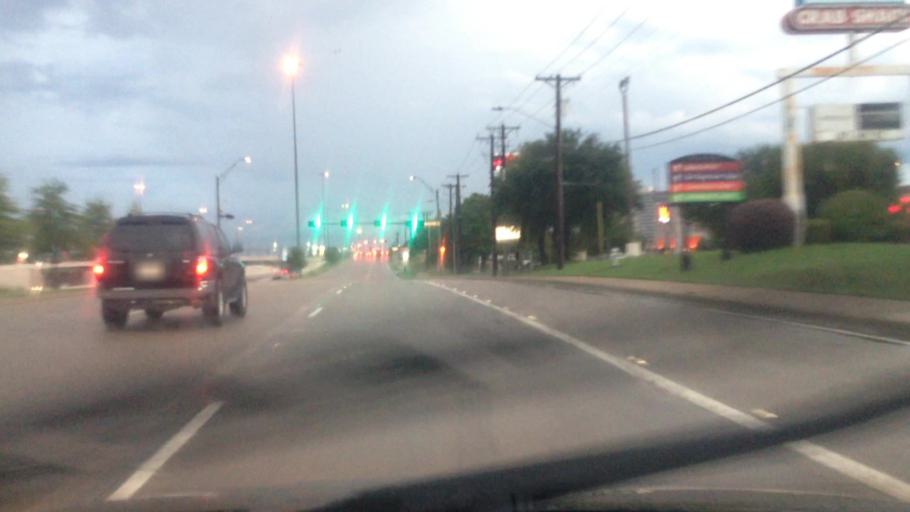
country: US
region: Texas
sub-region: Tarrant County
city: Arlington
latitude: 32.7590
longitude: -97.0895
